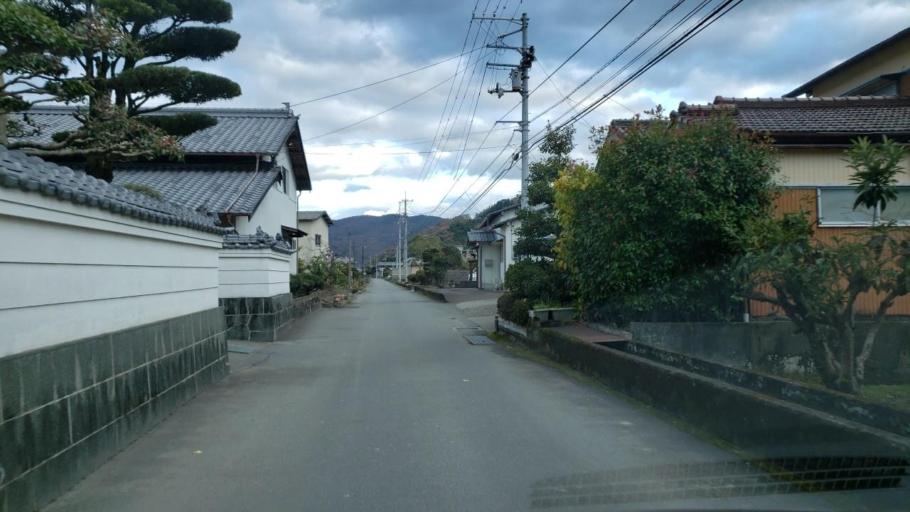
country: JP
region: Tokushima
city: Wakimachi
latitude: 34.0572
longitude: 134.1468
